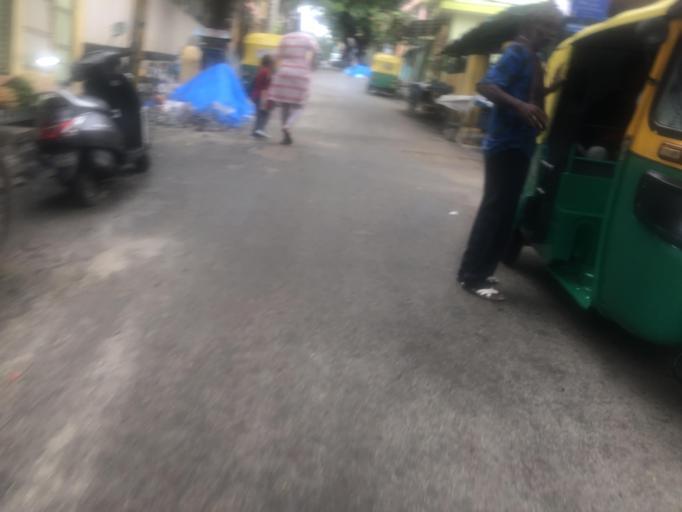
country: IN
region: Karnataka
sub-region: Bangalore Urban
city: Bangalore
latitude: 12.9409
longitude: 77.5383
